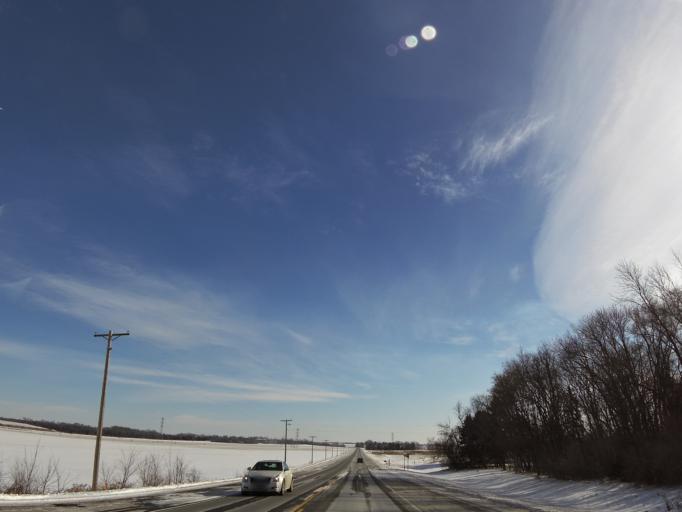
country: US
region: Minnesota
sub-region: Dakota County
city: Rosemount
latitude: 44.7389
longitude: -93.0198
